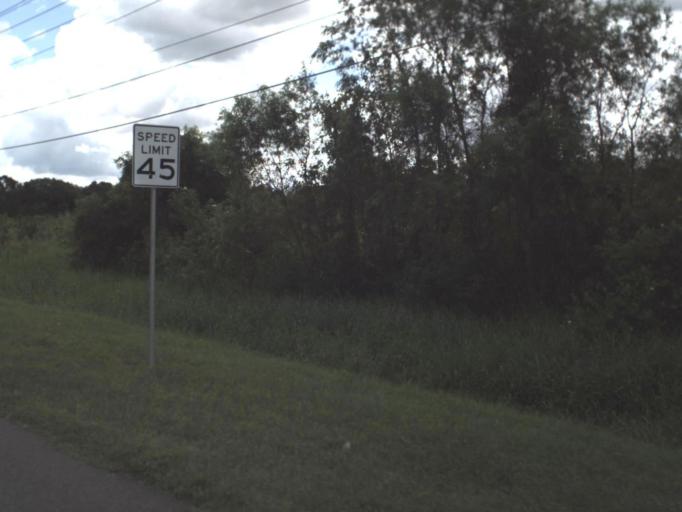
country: US
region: Florida
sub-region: Polk County
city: Winston
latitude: 28.0343
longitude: -82.0228
